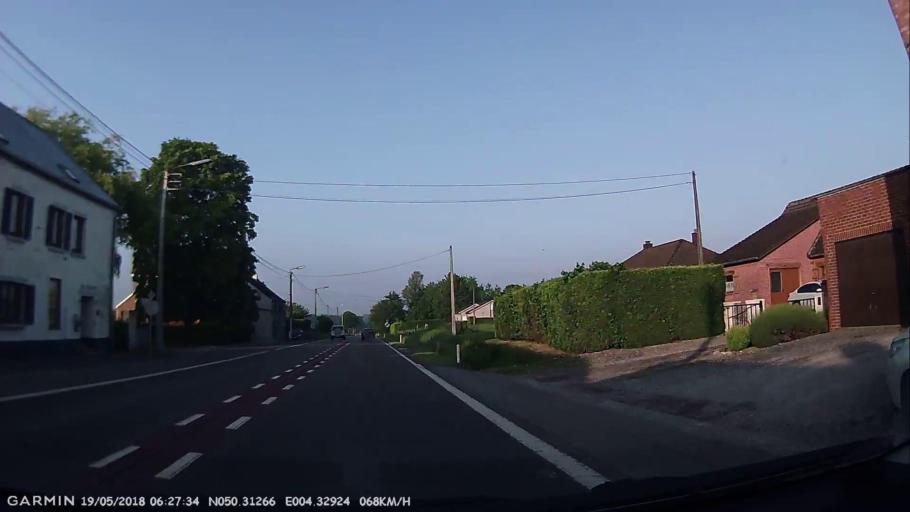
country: BE
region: Wallonia
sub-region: Province du Hainaut
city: Thuin
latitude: 50.3126
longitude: 4.3285
